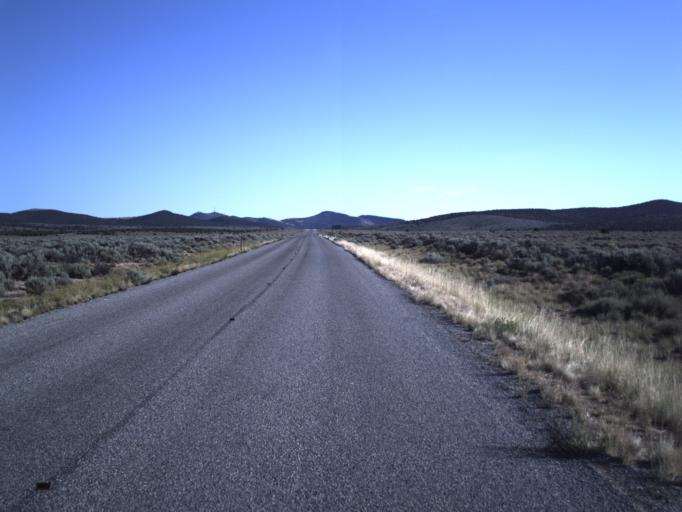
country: US
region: Utah
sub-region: Iron County
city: Enoch
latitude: 38.0036
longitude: -112.9977
